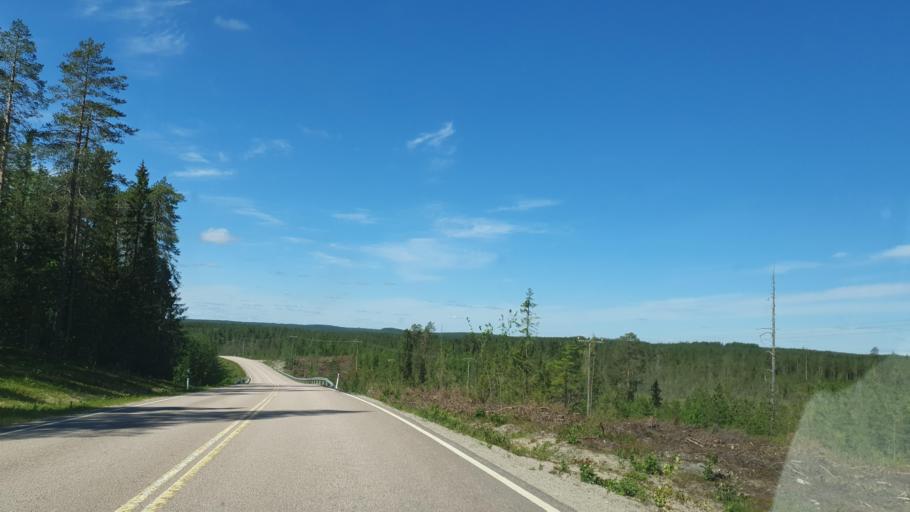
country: FI
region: Kainuu
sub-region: Kehys-Kainuu
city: Kuhmo
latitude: 64.4613
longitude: 29.5713
